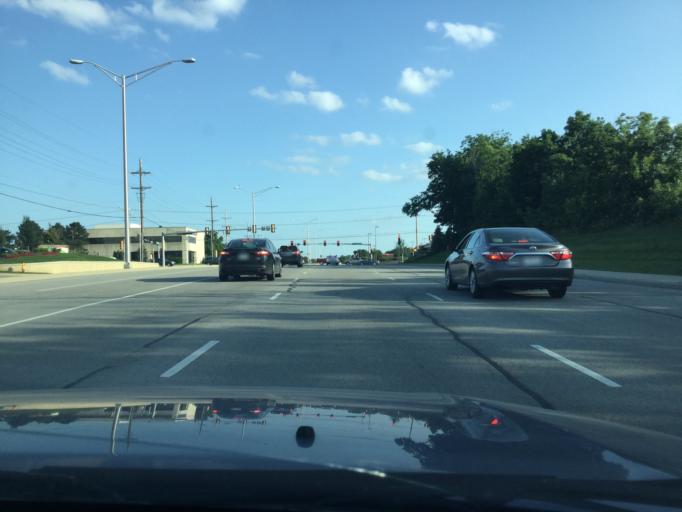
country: US
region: Kansas
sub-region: Johnson County
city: Lenexa
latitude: 38.9288
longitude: -94.6864
